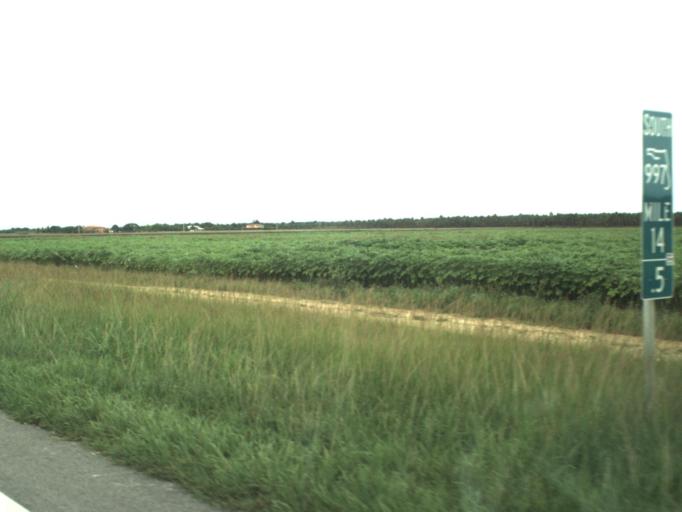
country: US
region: Florida
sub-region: Miami-Dade County
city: The Hammocks
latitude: 25.6466
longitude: -80.4803
